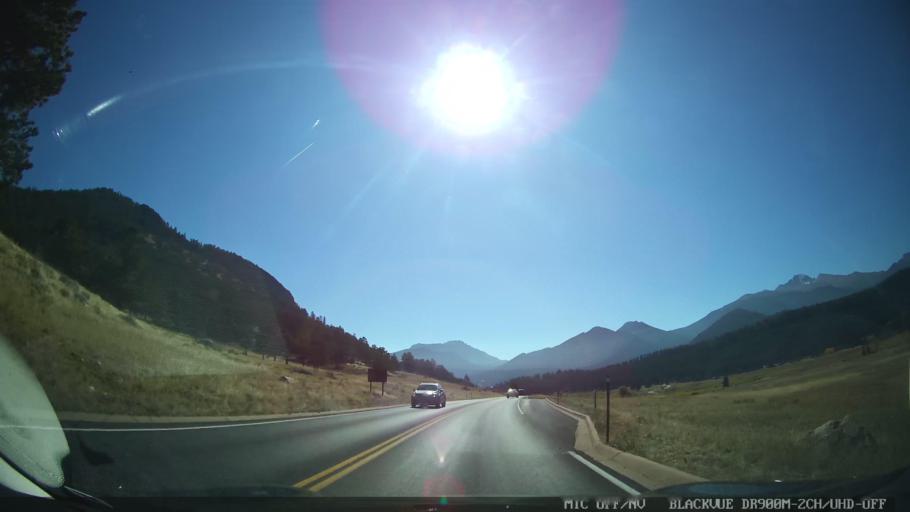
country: US
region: Colorado
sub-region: Larimer County
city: Estes Park
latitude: 40.3558
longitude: -105.5849
